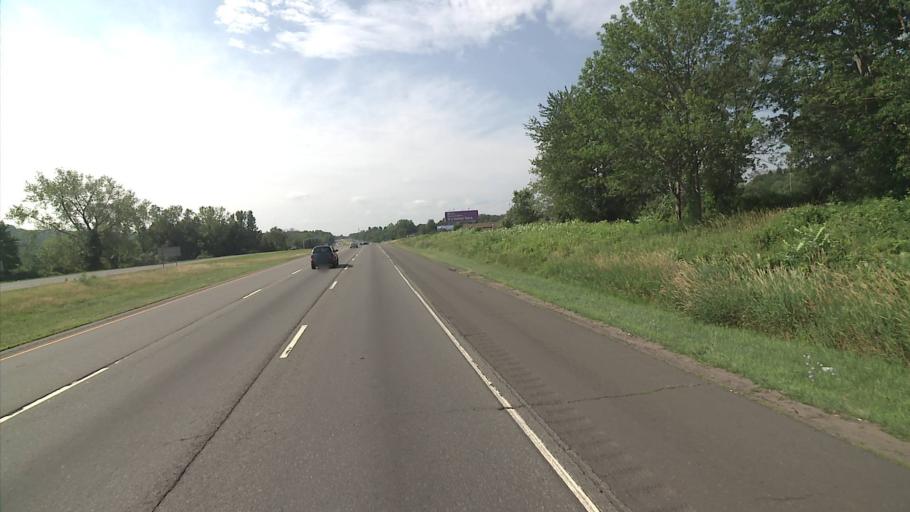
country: US
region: Connecticut
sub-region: New Haven County
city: Meriden
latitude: 41.5089
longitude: -72.7697
